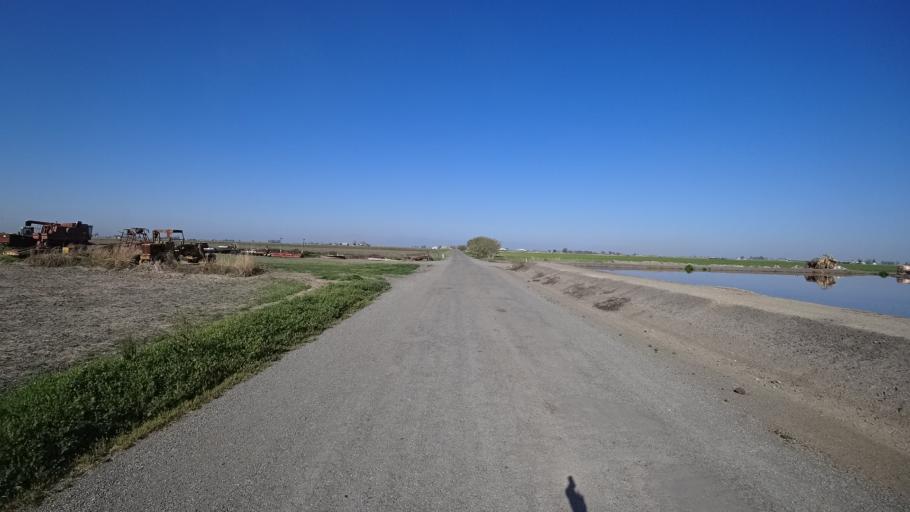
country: US
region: California
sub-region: Glenn County
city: Willows
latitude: 39.5726
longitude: -122.0690
